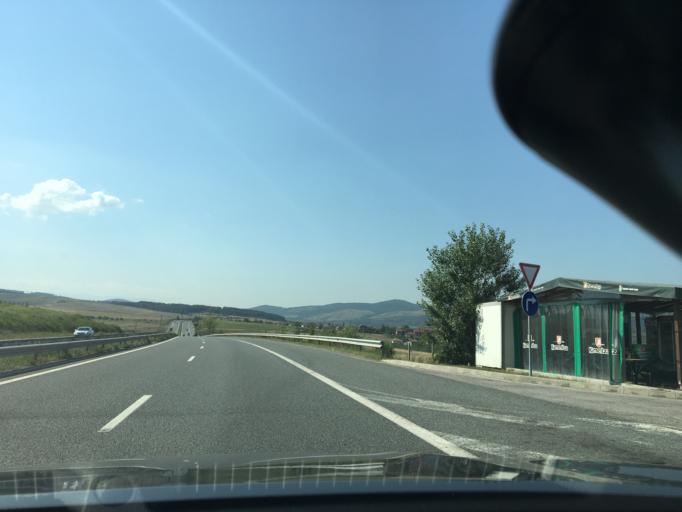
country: BG
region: Pernik
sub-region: Obshtina Pernik
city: Pernik
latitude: 42.5890
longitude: 23.1198
